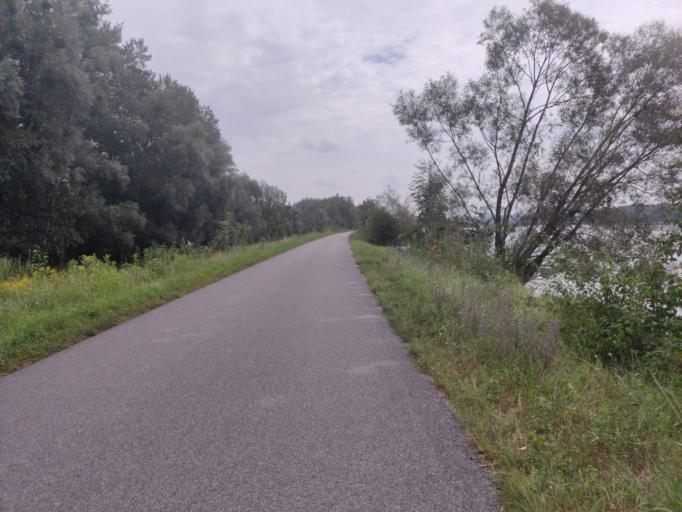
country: AT
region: Upper Austria
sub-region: Politischer Bezirk Perg
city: Perg
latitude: 48.1937
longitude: 14.6200
